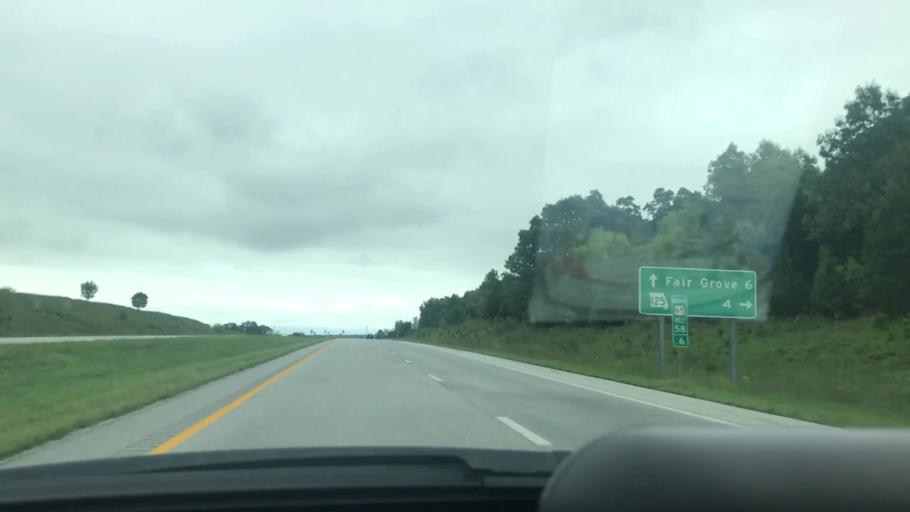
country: US
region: Missouri
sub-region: Greene County
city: Strafford
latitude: 37.2982
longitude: -93.1784
